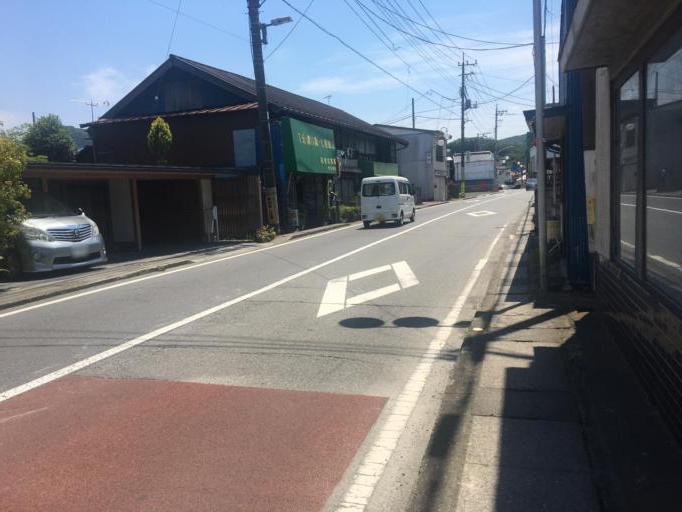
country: JP
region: Saitama
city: Ogawa
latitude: 36.0557
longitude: 139.2592
